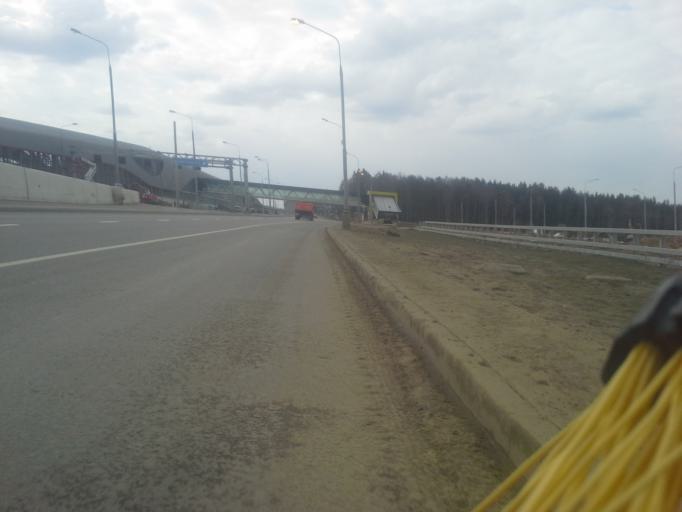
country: RU
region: Moscow
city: Solntsevo
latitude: 55.5999
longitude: 37.4113
